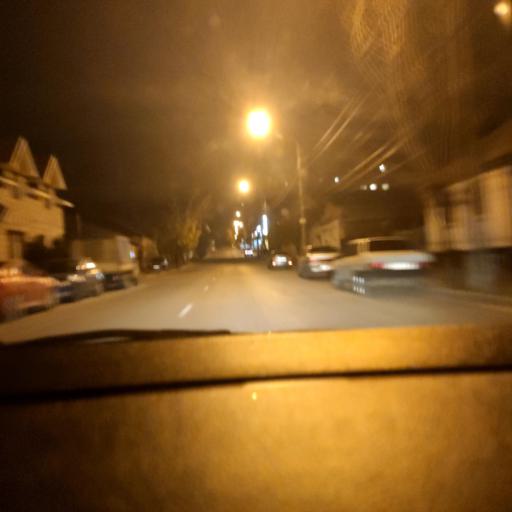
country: RU
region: Voronezj
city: Voronezh
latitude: 51.6799
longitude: 39.2198
